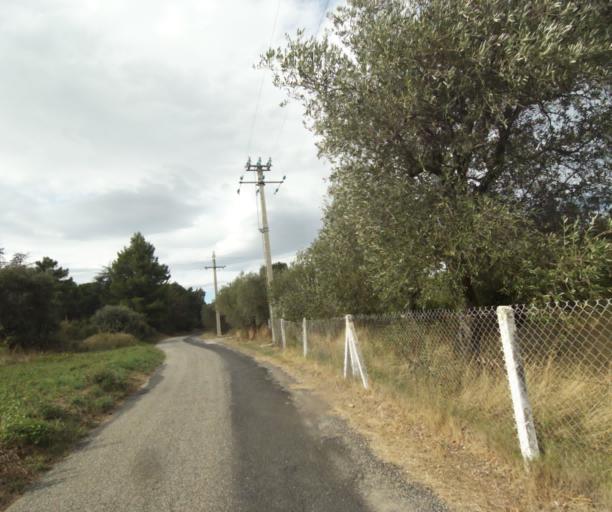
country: FR
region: Languedoc-Roussillon
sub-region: Departement des Pyrenees-Orientales
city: Argelers
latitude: 42.5461
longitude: 2.9987
